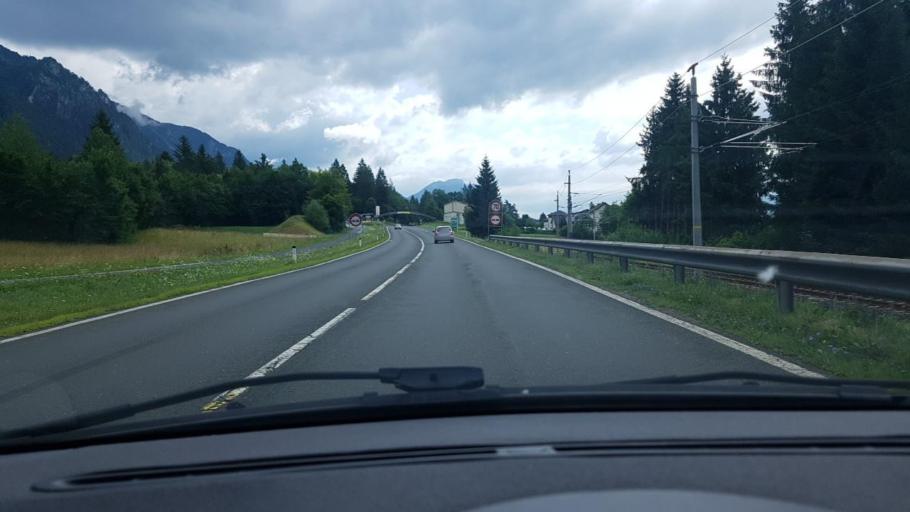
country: AT
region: Carinthia
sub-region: Politischer Bezirk Hermagor
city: Hermagor
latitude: 46.6320
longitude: 13.4425
